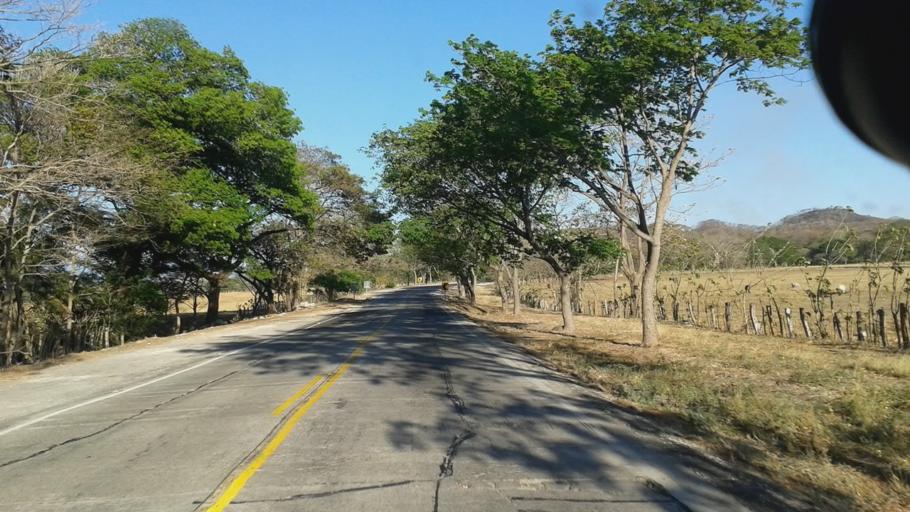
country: CR
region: Guanacaste
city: Nandayure
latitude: 10.2257
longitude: -85.1674
